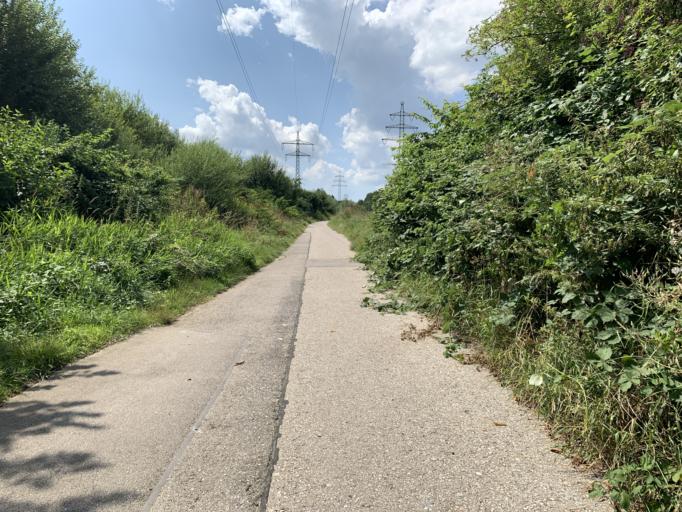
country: DE
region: Bavaria
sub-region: Upper Bavaria
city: Freising
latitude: 48.4130
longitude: 11.7520
